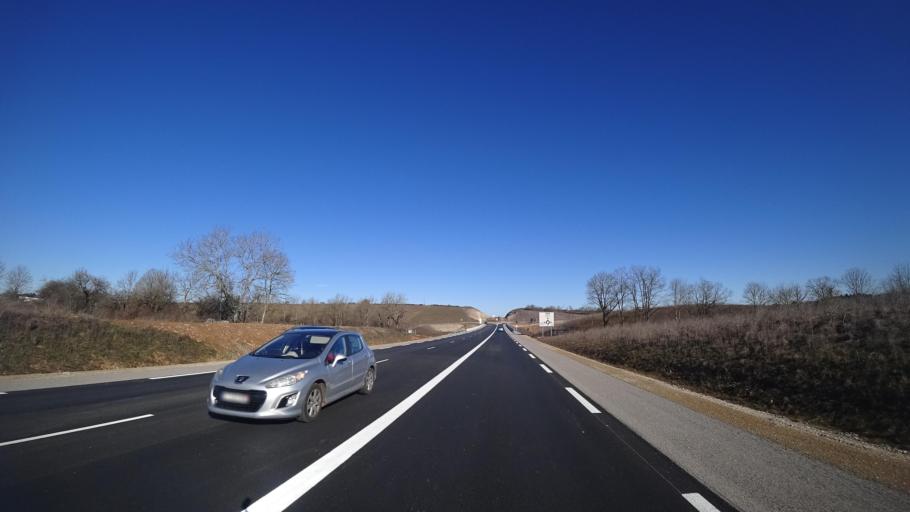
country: FR
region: Midi-Pyrenees
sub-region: Departement de l'Aveyron
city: Sebazac-Concoures
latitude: 44.3980
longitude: 2.6175
